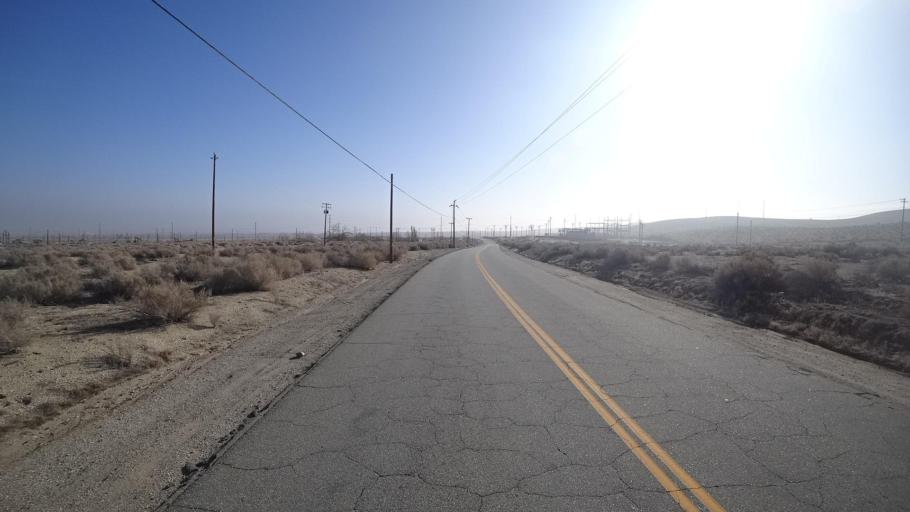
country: US
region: California
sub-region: Kern County
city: Taft Heights
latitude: 35.1954
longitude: -119.5846
